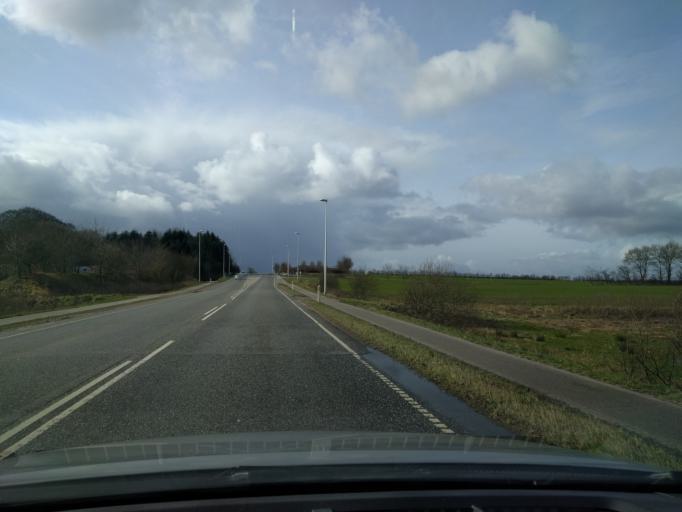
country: DK
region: South Denmark
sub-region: Kolding Kommune
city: Lunderskov
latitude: 55.4488
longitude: 9.3672
